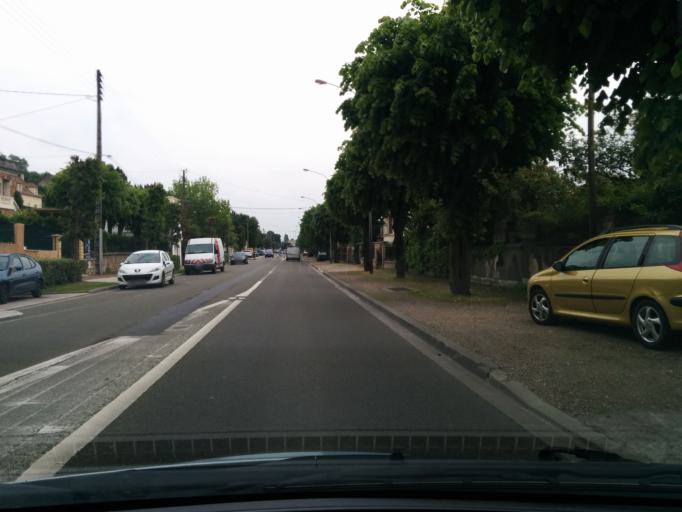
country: FR
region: Ile-de-France
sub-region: Departement des Yvelines
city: Juziers
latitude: 48.9904
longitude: 1.8505
